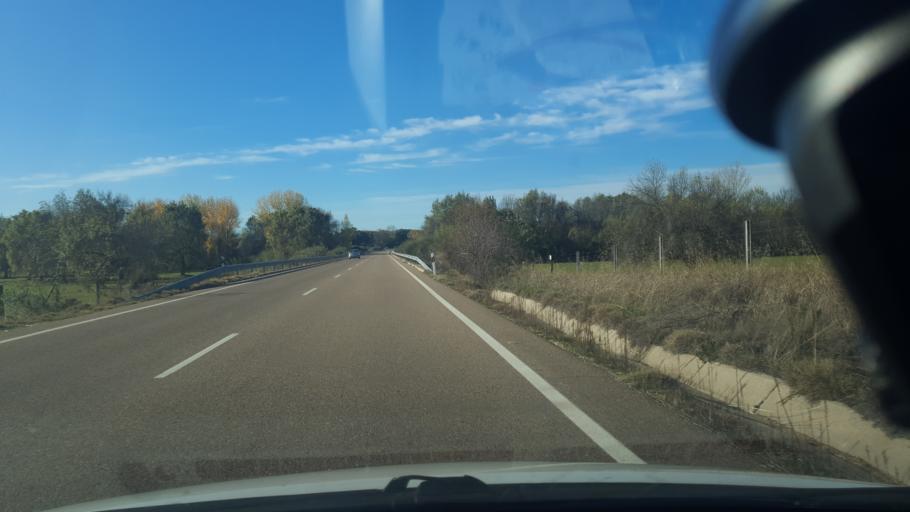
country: ES
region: Castille and Leon
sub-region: Provincia de Avila
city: Candeleda
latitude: 40.1420
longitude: -5.2027
